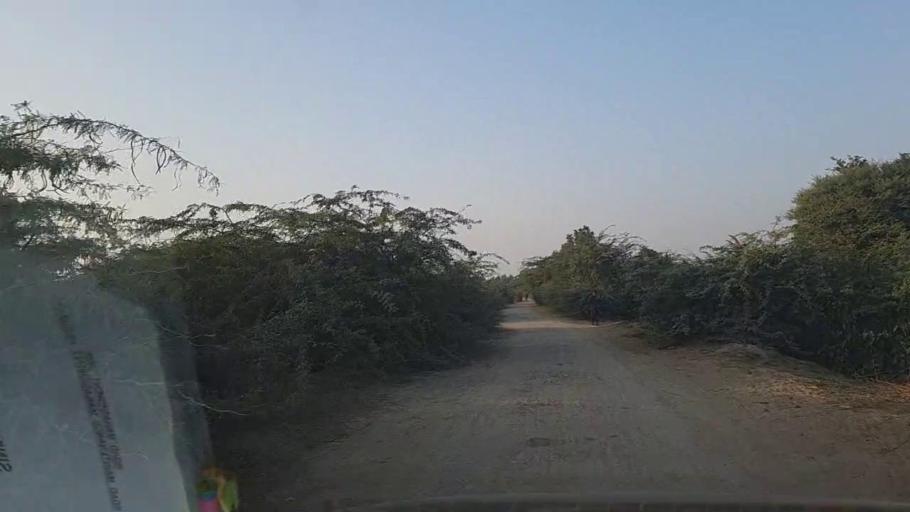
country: PK
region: Sindh
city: Keti Bandar
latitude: 24.3118
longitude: 67.6007
